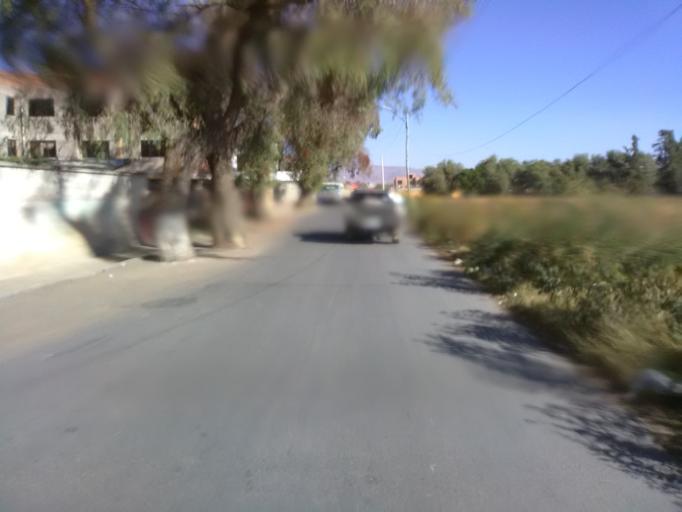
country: BO
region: Cochabamba
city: Cochabamba
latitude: -17.3795
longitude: -66.2008
